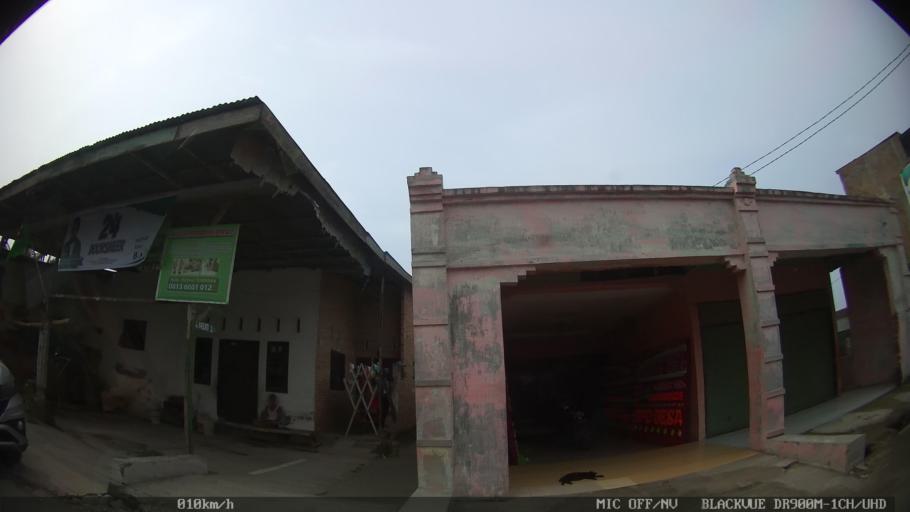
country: ID
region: North Sumatra
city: Medan
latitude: 3.5695
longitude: 98.7527
